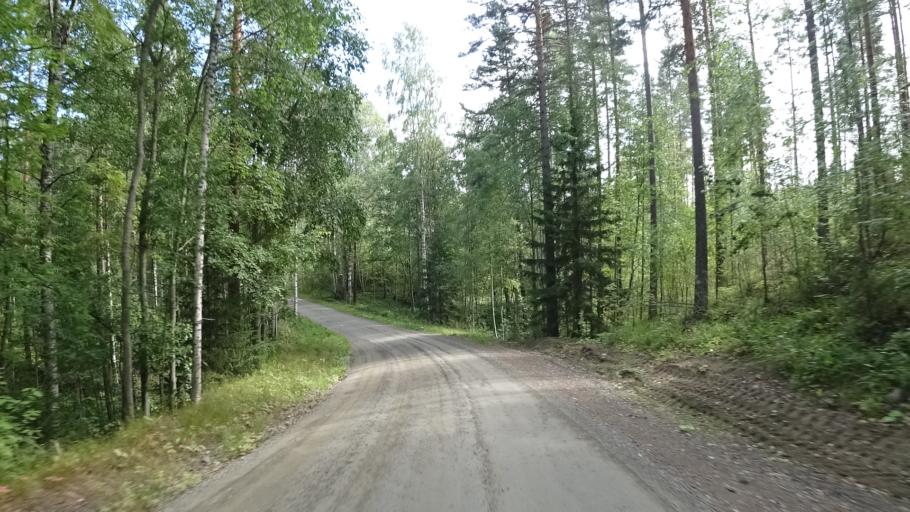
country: FI
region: North Karelia
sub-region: Joensuu
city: Pyhaeselkae
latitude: 62.3734
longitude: 29.8210
